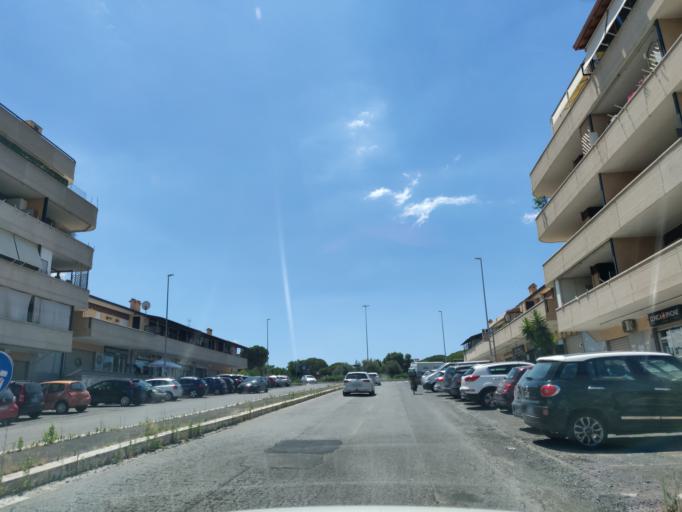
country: IT
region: Latium
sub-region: Citta metropolitana di Roma Capitale
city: Setteville
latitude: 41.9112
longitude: 12.6617
